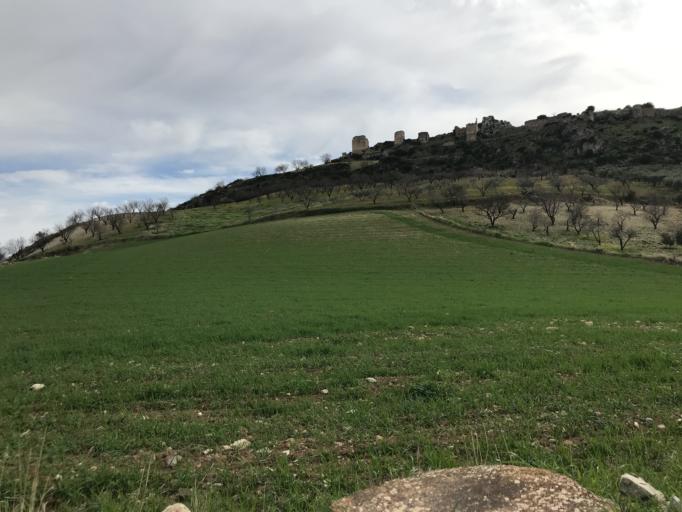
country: ES
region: Andalusia
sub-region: Provincia de Malaga
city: Ardales
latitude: 36.8721
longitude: -4.8816
